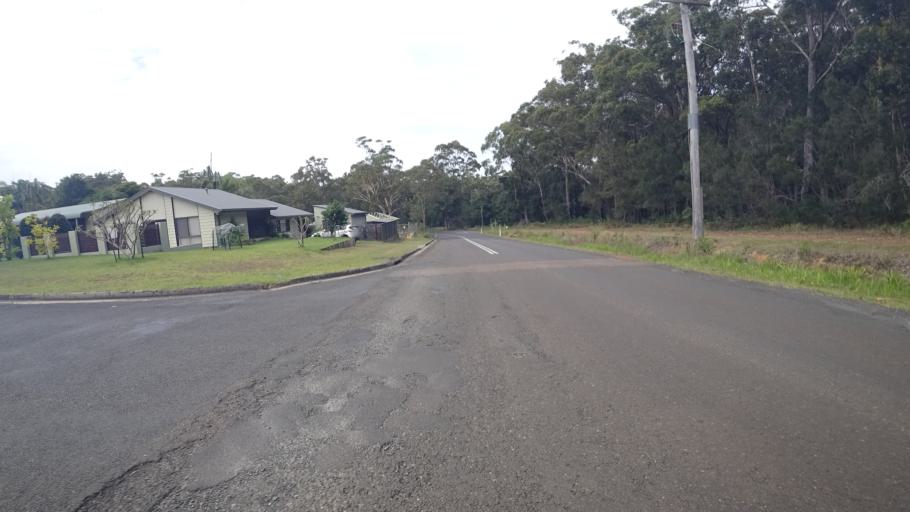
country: AU
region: New South Wales
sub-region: Shoalhaven Shire
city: Milton
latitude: -35.2589
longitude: 150.5051
